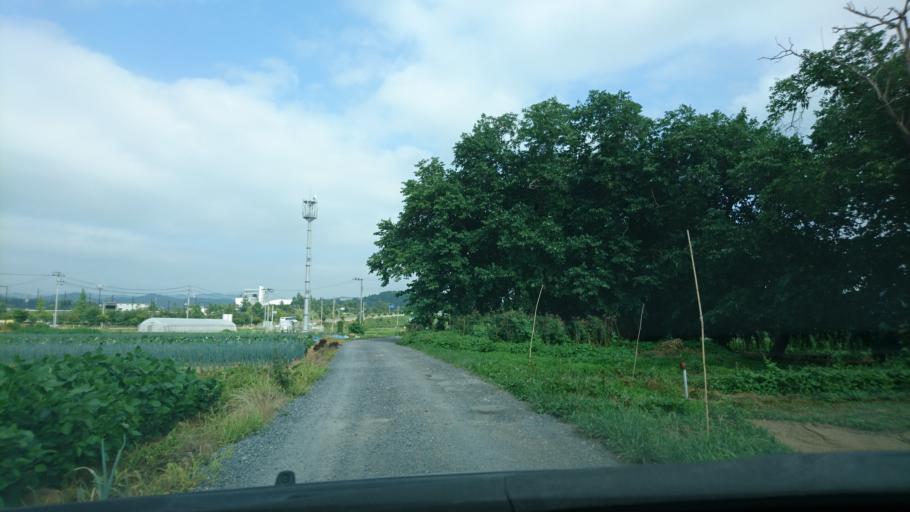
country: JP
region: Iwate
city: Ichinoseki
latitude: 38.9374
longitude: 141.1539
